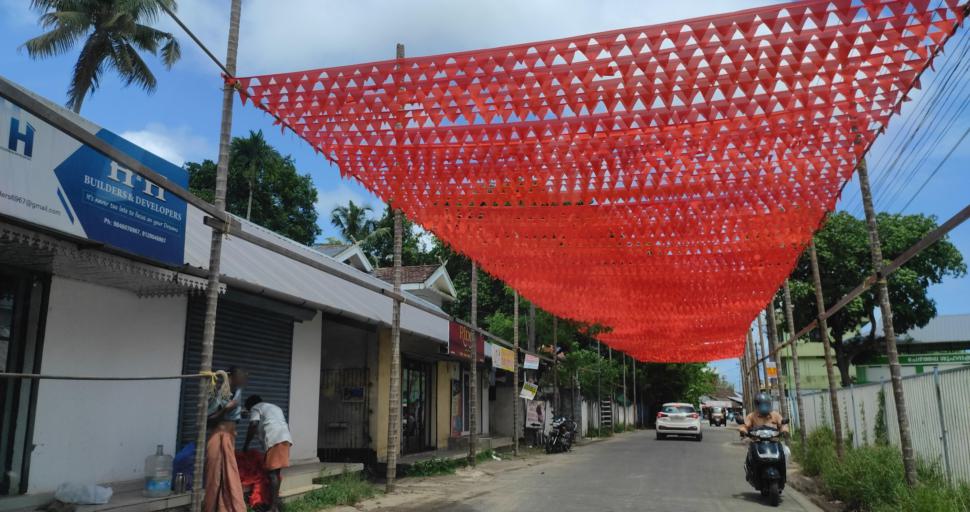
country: IN
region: Kerala
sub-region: Alappuzha
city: Vayalar
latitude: 9.6932
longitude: 76.3374
